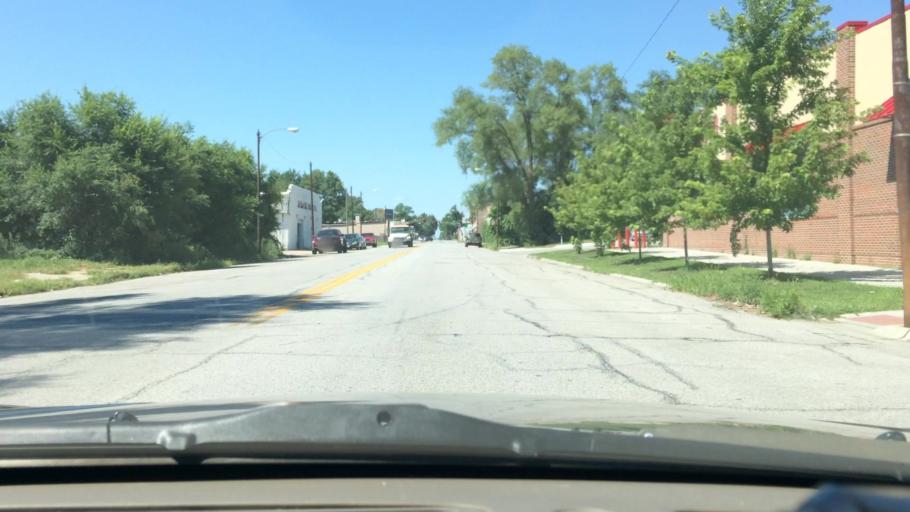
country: US
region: Iowa
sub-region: Pottawattamie County
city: Carter Lake
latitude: 41.2829
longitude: -95.9373
